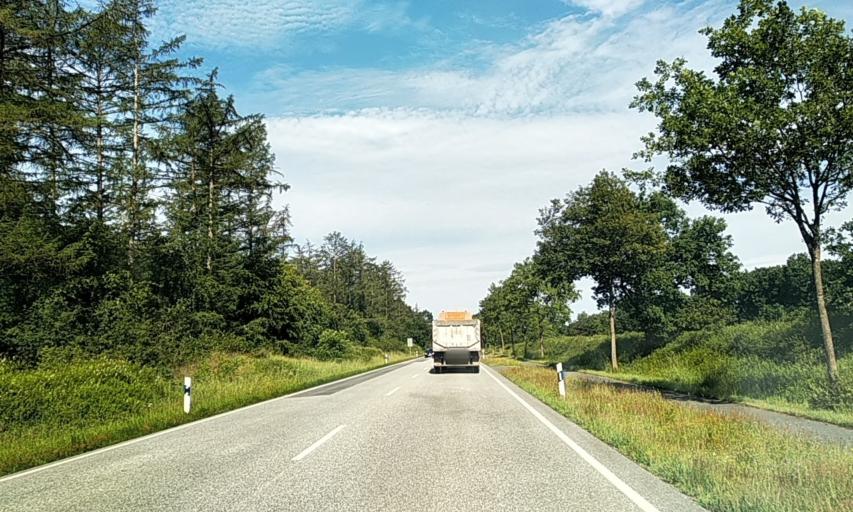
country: DE
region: Schleswig-Holstein
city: Lohe-Fohrden
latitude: 54.3507
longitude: 9.5702
